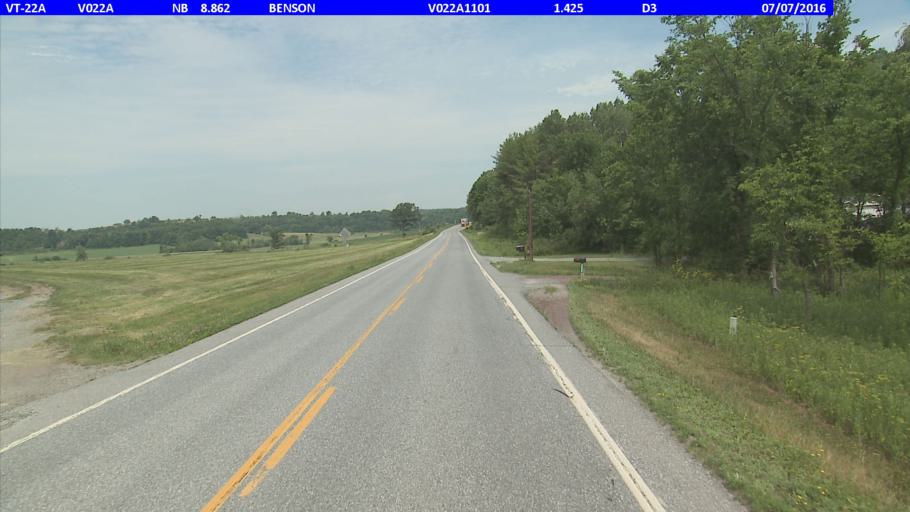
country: US
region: Vermont
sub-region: Rutland County
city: Fair Haven
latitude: 43.6896
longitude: -73.2907
